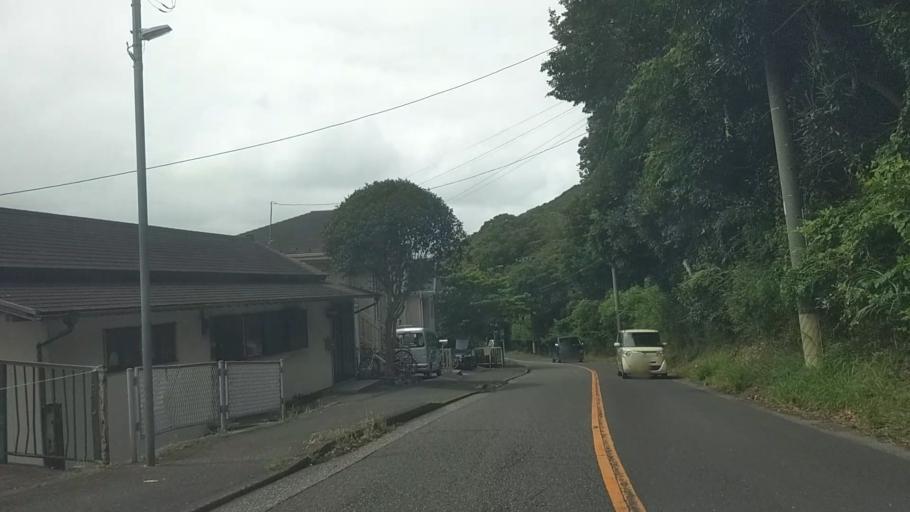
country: JP
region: Kanagawa
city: Yokosuka
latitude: 35.2583
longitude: 139.7184
